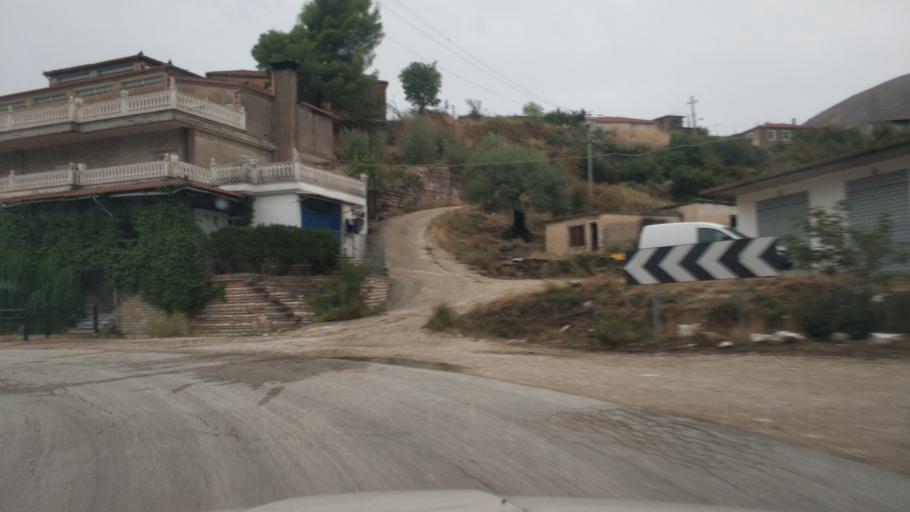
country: AL
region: Vlore
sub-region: Rrethi i Delvines
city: Mesopotam
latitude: 39.9176
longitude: 20.1356
